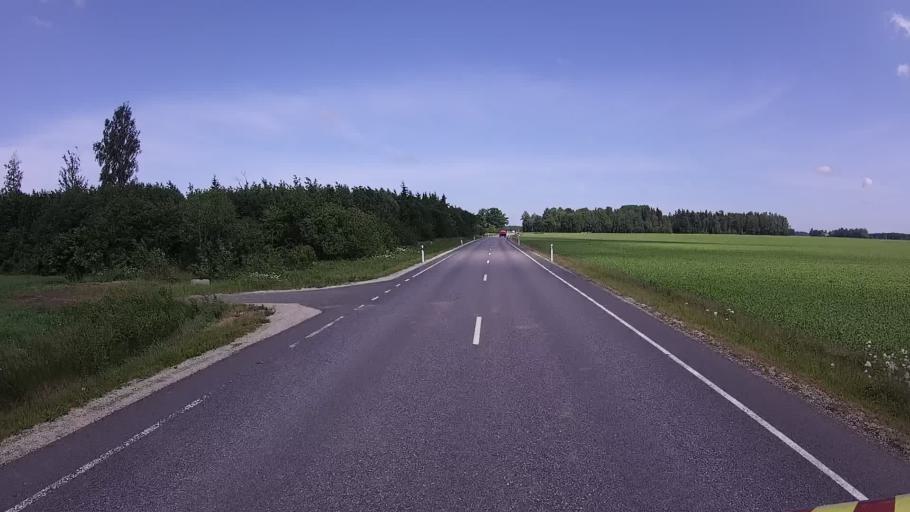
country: EE
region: Tartu
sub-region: Tartu linn
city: Tartu
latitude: 58.3885
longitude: 26.8902
